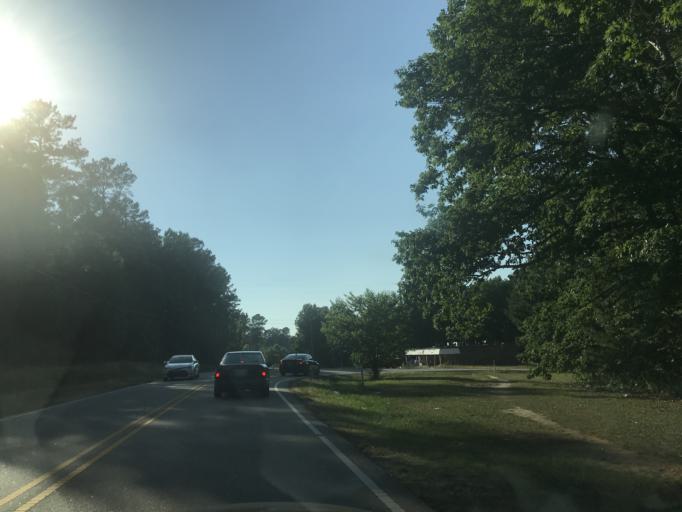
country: US
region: North Carolina
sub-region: Wake County
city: Garner
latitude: 35.7355
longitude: -78.6065
